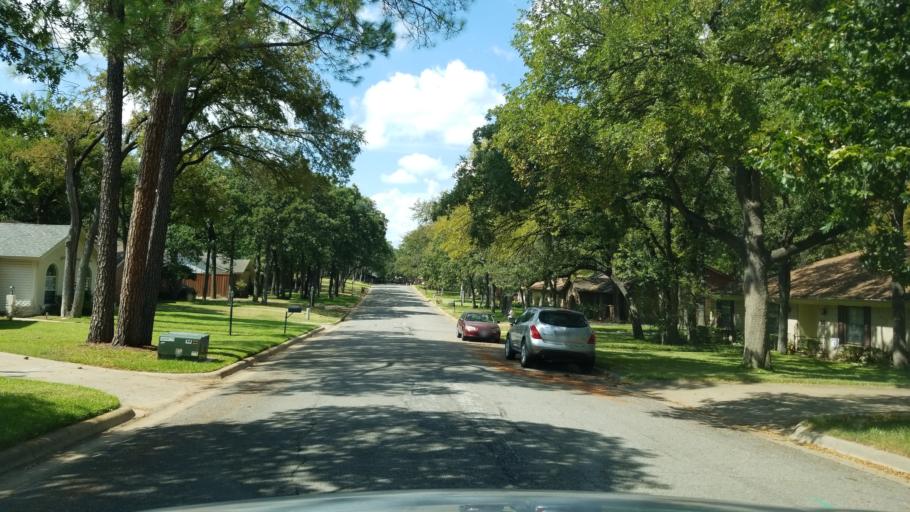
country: US
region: Texas
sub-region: Tarrant County
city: Euless
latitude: 32.8583
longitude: -97.0837
